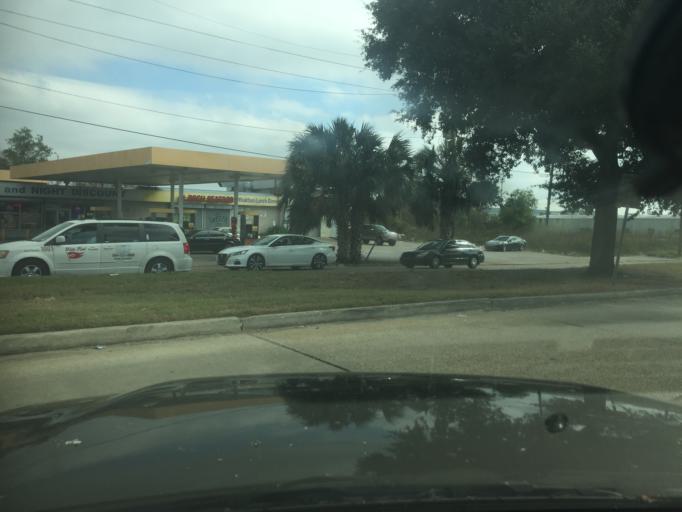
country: US
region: Louisiana
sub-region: Saint Bernard Parish
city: Arabi
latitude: 30.0019
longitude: -90.0355
